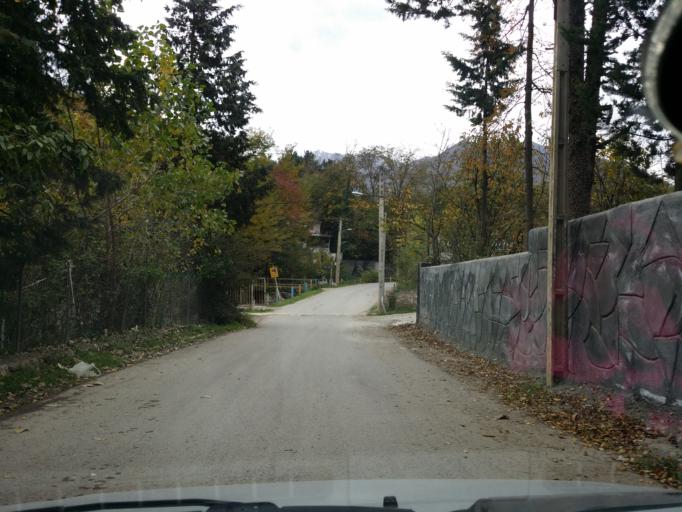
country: IR
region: Mazandaran
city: `Abbasabad
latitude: 36.5016
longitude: 51.1481
